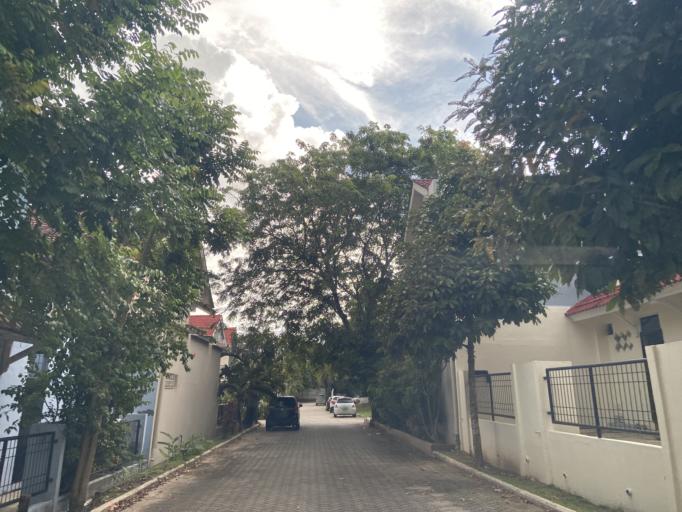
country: SG
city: Singapore
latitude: 1.1217
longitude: 104.0234
